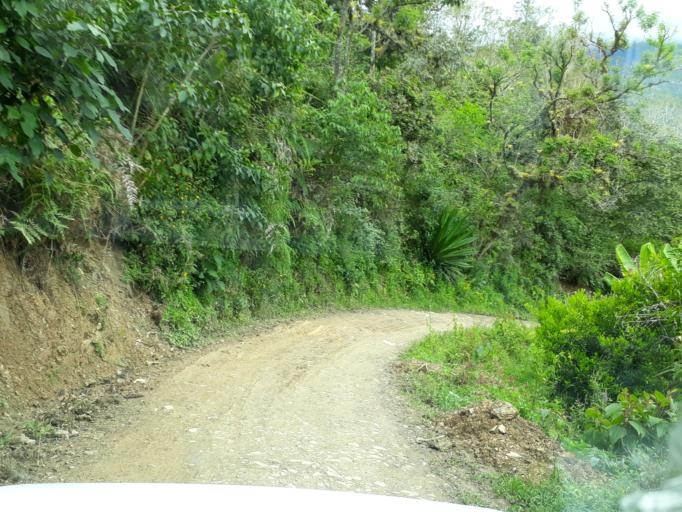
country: CO
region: Cundinamarca
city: Gacheta
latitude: 4.8142
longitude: -73.6426
